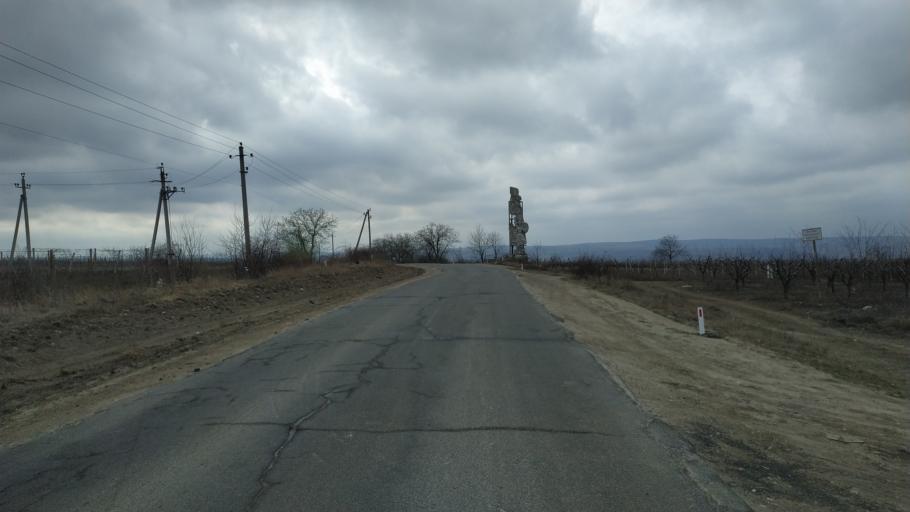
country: MD
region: Laloveni
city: Ialoveni
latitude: 46.9039
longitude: 28.7764
